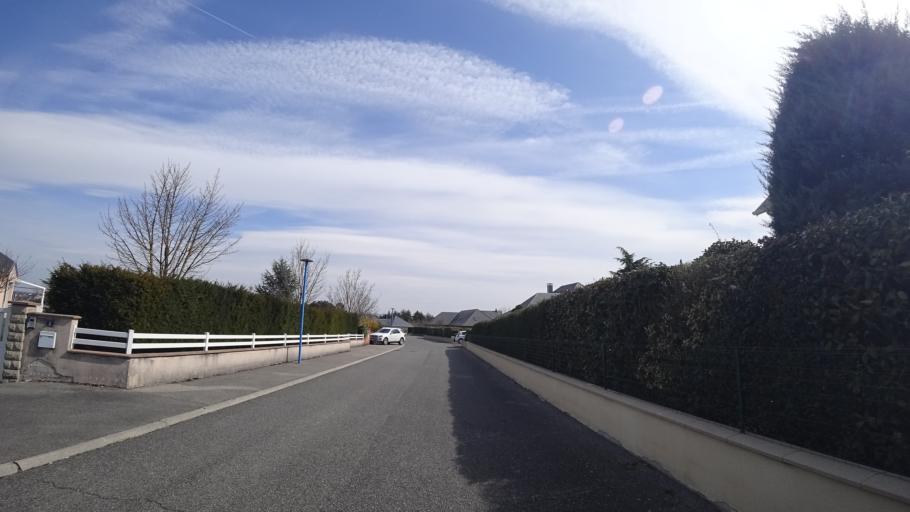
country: FR
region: Midi-Pyrenees
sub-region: Departement de l'Aveyron
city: Olemps
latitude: 44.3734
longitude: 2.5550
